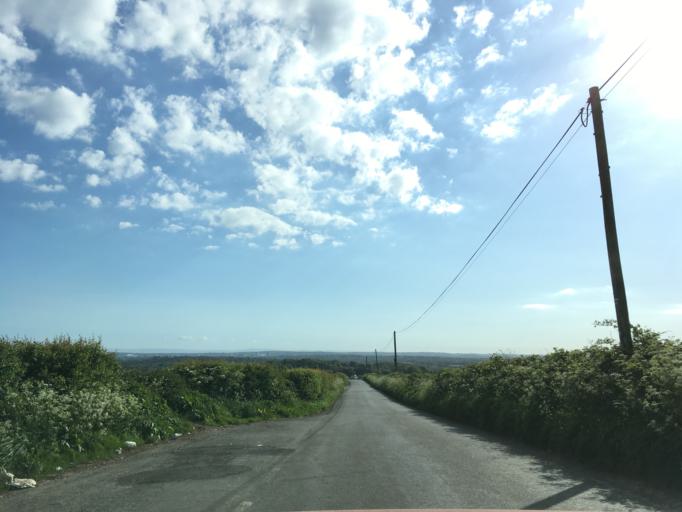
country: GB
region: Wales
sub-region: Newport
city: Marshfield
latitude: 51.5558
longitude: -3.0782
